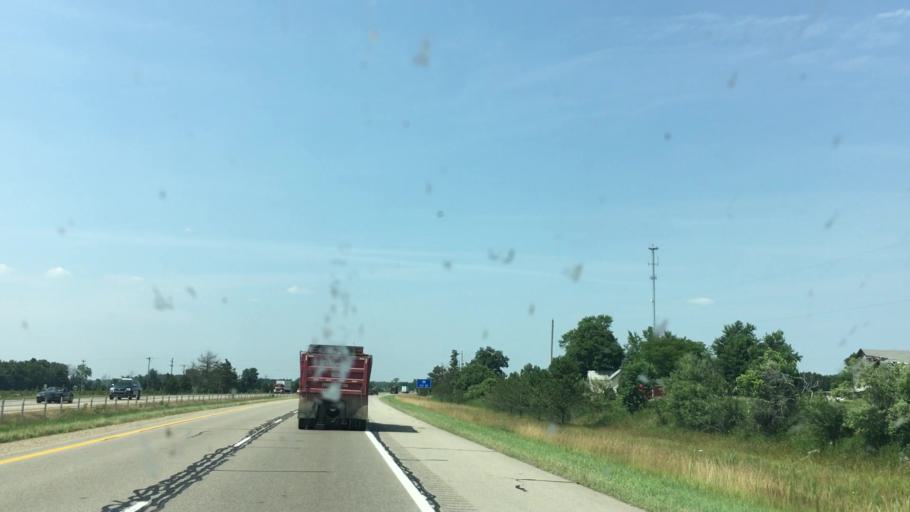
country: US
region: Michigan
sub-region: Allegan County
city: Wayland
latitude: 42.6174
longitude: -85.6618
